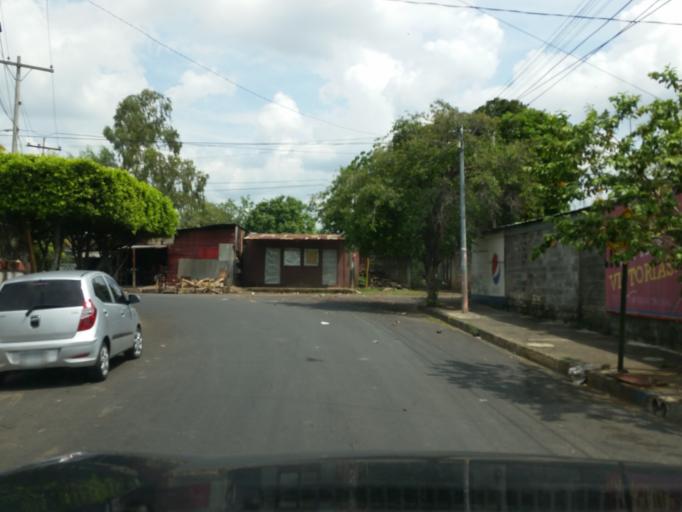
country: NI
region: Managua
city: Managua
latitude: 12.1395
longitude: -86.2927
